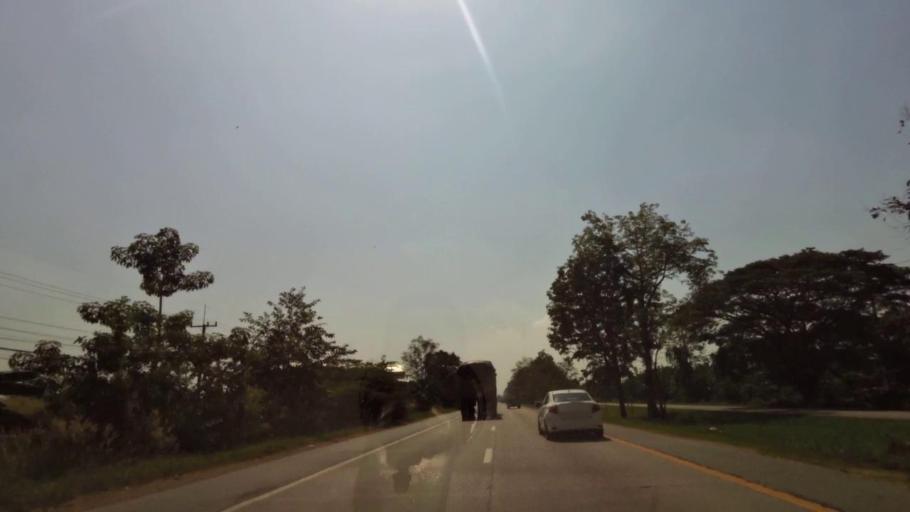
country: TH
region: Phichit
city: Wachira Barami
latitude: 16.6042
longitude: 100.1483
